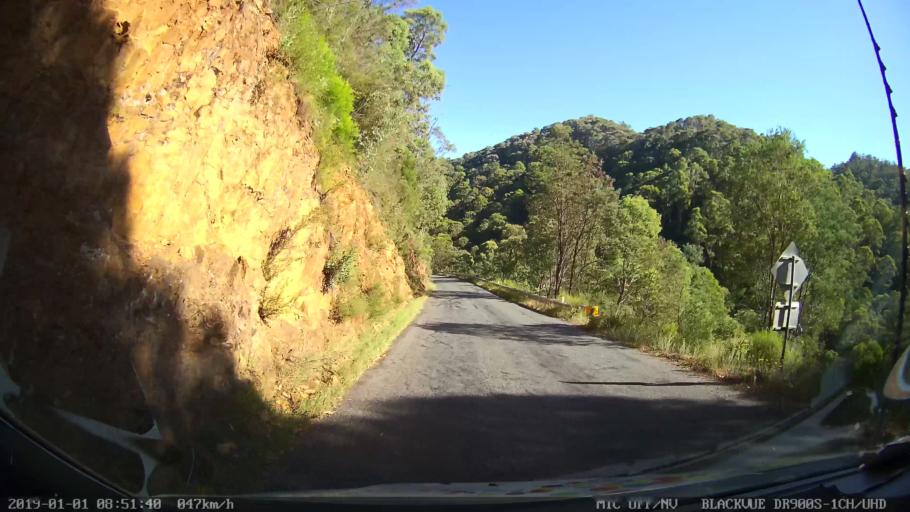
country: AU
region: New South Wales
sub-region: Snowy River
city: Jindabyne
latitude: -36.2701
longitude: 148.2017
